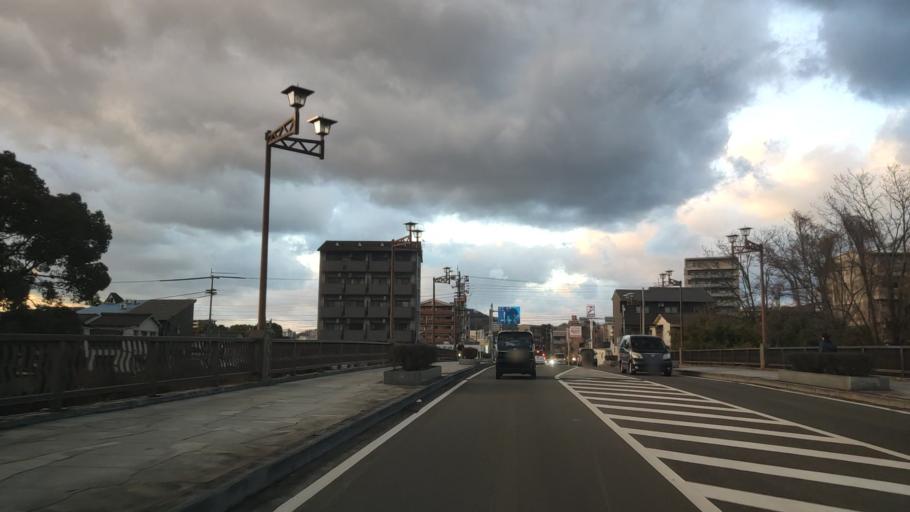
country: JP
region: Ehime
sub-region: Shikoku-chuo Shi
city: Matsuyama
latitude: 33.8394
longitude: 132.7859
